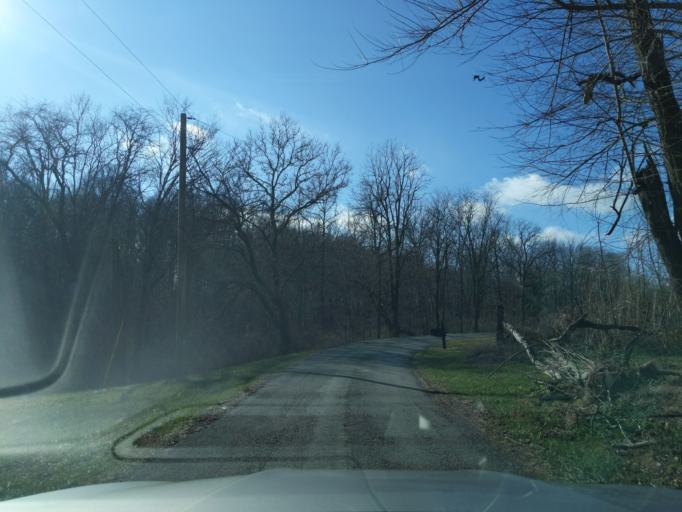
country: US
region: Indiana
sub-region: Decatur County
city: Greensburg
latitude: 39.2417
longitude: -85.4648
